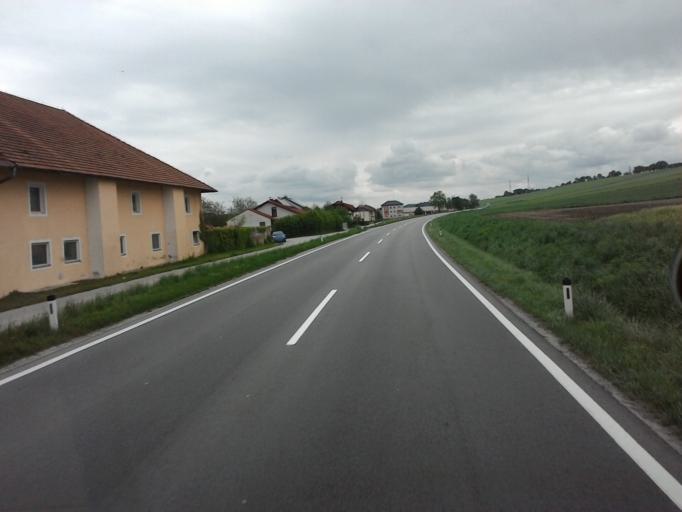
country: AT
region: Upper Austria
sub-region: Politischer Bezirk Grieskirchen
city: Grieskirchen
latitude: 48.2325
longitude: 13.8008
